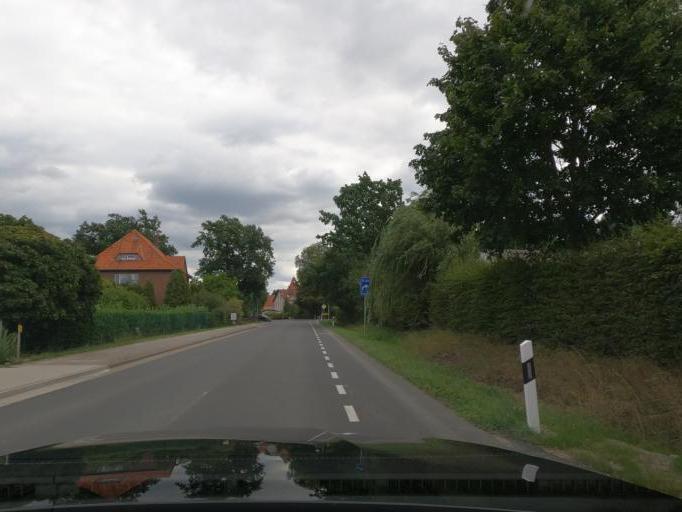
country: DE
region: Lower Saxony
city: Hohenhameln
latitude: 52.3076
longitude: 10.0428
